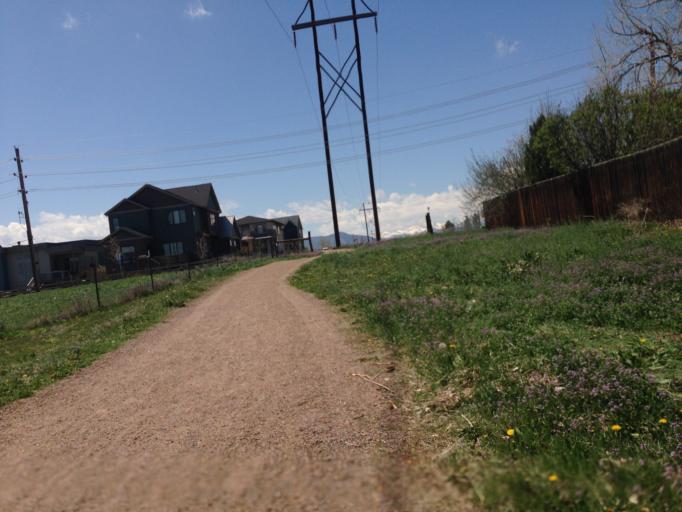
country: US
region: Colorado
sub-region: Boulder County
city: Louisville
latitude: 39.9906
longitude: -105.1180
